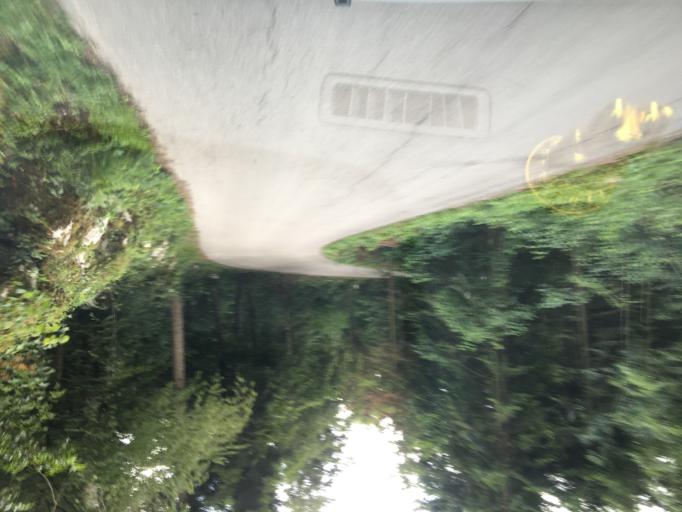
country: SI
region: Postojna
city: Postojna
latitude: 45.8030
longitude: 14.2018
